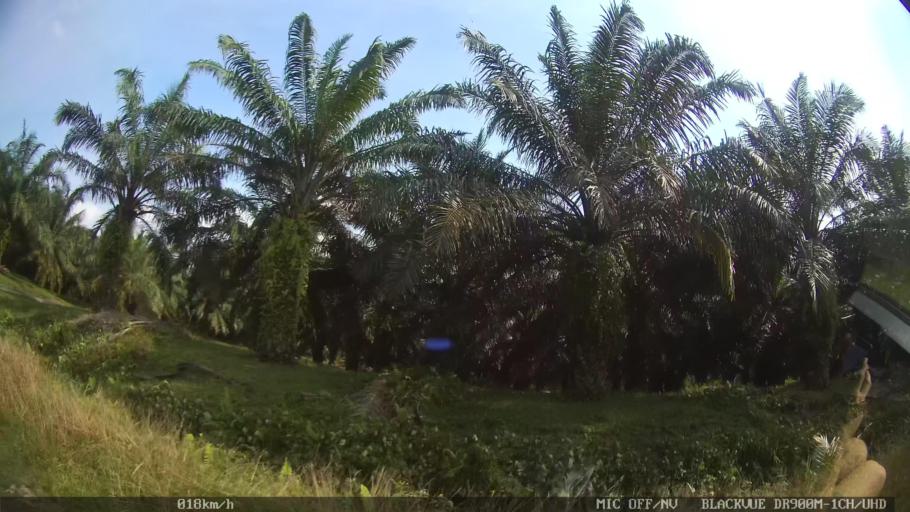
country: ID
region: North Sumatra
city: Binjai
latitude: 3.6426
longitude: 98.5250
